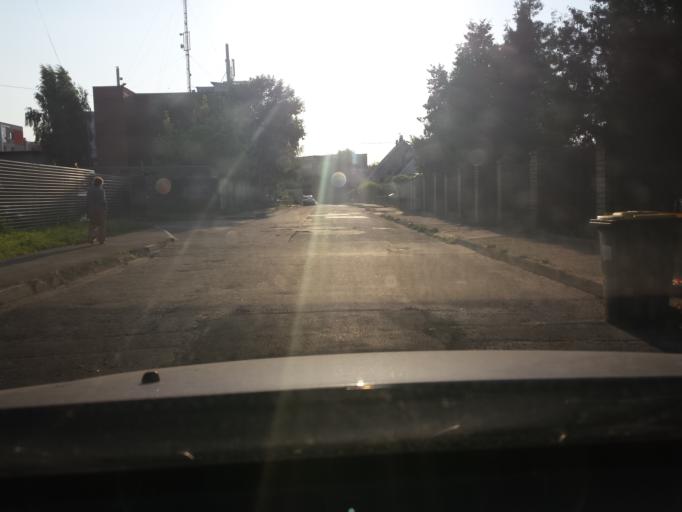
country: LV
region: Riga
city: Jaunciems
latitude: 56.9721
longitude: 24.1822
